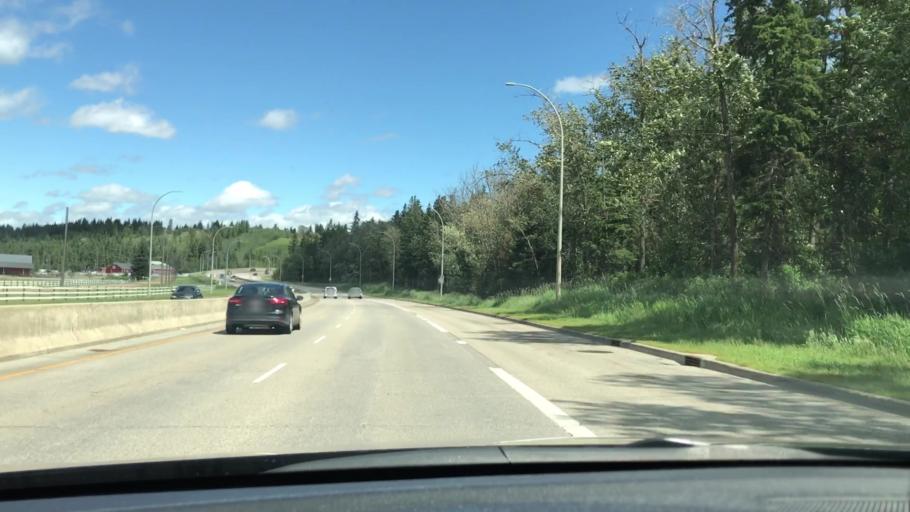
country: CA
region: Alberta
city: Edmonton
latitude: 53.5036
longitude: -113.5518
